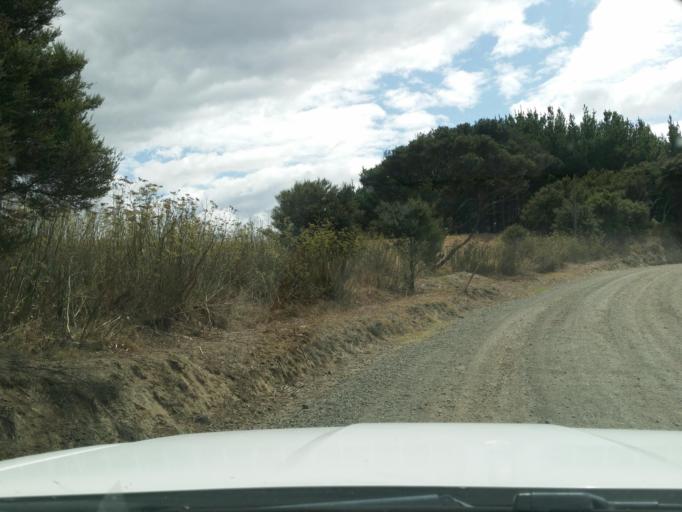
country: NZ
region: Auckland
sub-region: Auckland
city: Wellsford
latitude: -36.3338
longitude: 174.1552
